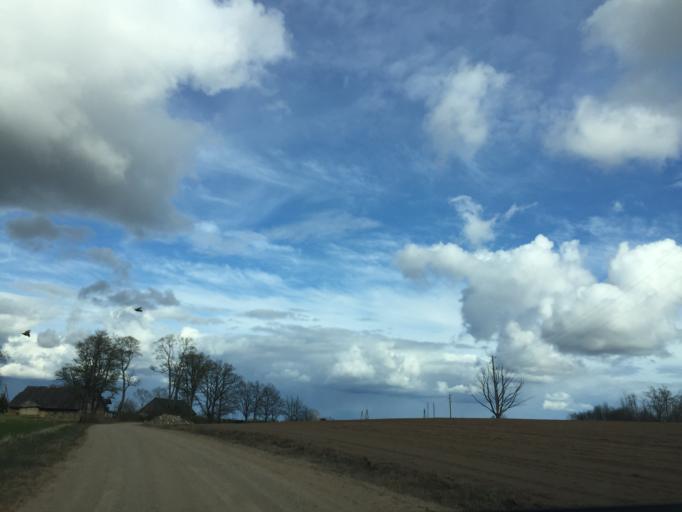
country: LV
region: Burtnieki
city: Matisi
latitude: 57.6123
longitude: 25.0178
